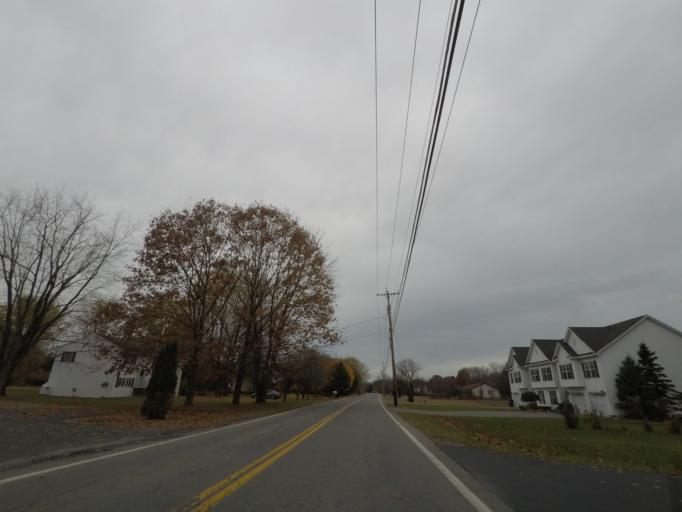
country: US
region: New York
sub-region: Saratoga County
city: Mechanicville
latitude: 42.8477
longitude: -73.6870
